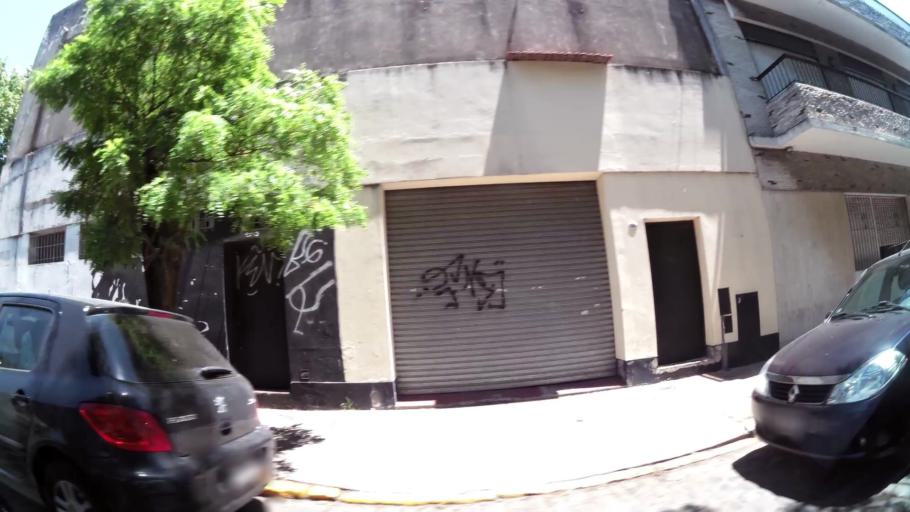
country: AR
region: Buenos Aires
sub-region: Partido de Avellaneda
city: Avellaneda
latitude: -34.6532
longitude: -58.3847
